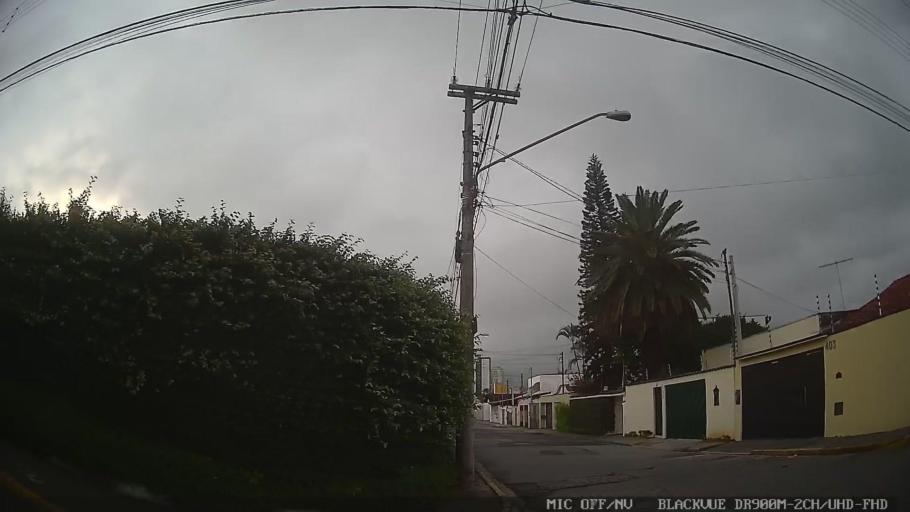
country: BR
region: Sao Paulo
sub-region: Mogi das Cruzes
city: Mogi das Cruzes
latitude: -23.5220
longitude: -46.1712
